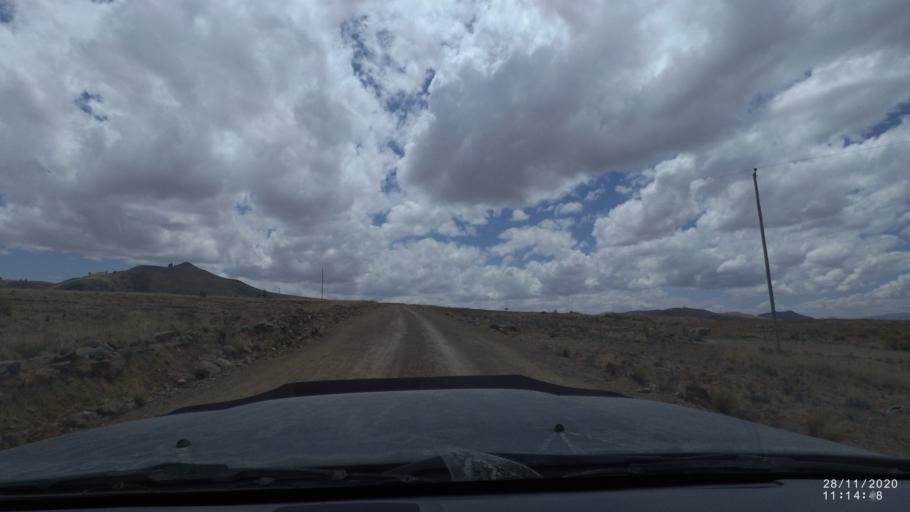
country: BO
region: Cochabamba
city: Tarata
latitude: -17.7456
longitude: -66.0949
